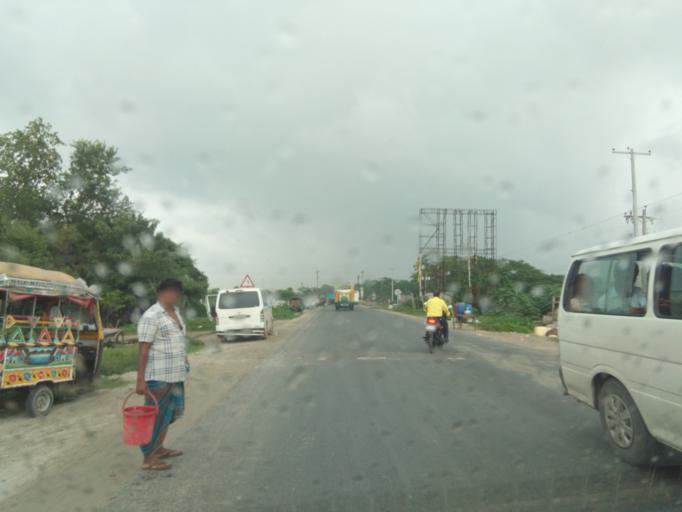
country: BD
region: Dhaka
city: Char Bhadrasan
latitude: 23.3693
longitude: 90.0705
